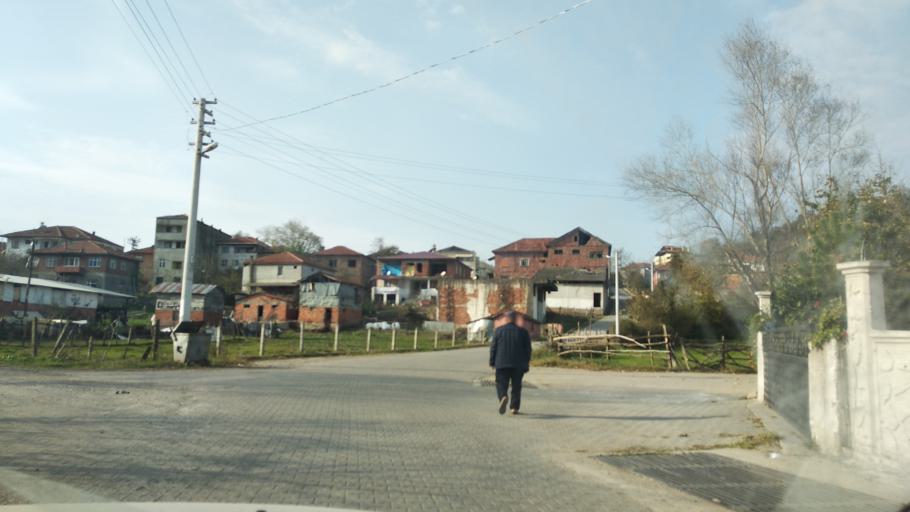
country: TR
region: Sakarya
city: Karasu
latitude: 41.0549
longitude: 30.6288
